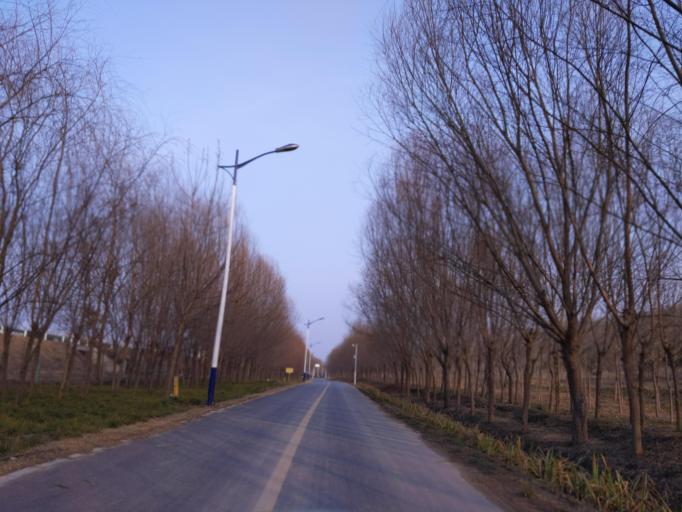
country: CN
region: Henan Sheng
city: Puyang
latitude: 35.8212
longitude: 115.0096
